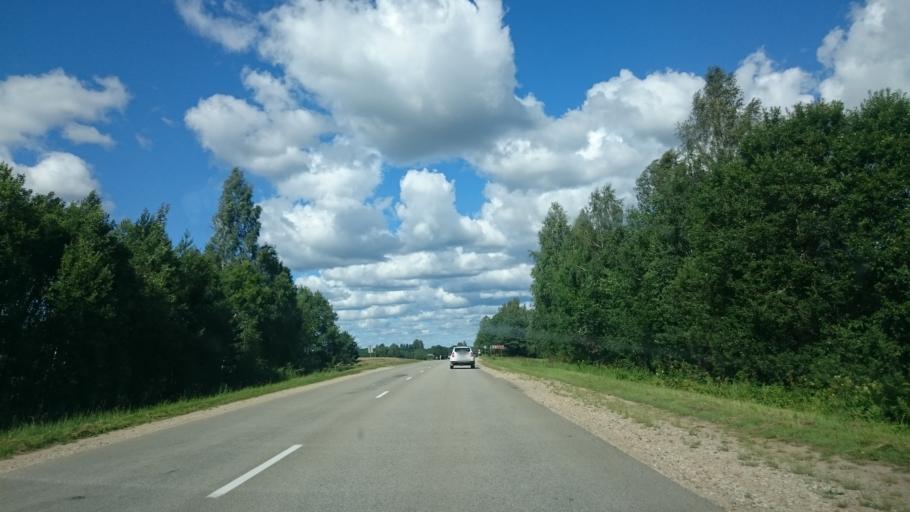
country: LV
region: Kuldigas Rajons
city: Kuldiga
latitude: 56.9541
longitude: 21.9415
